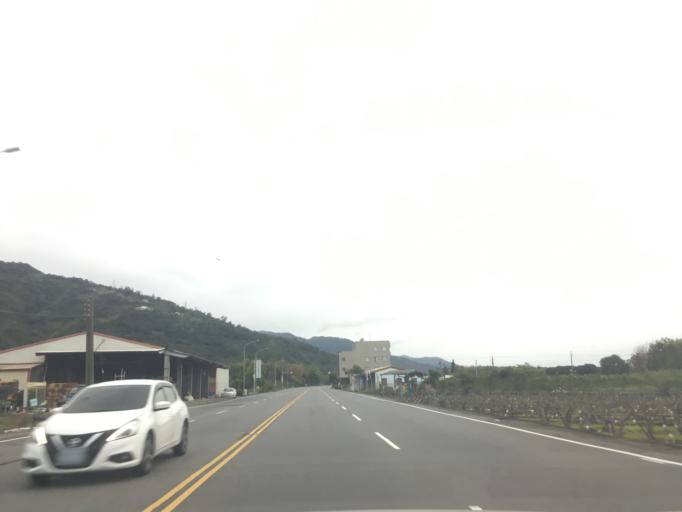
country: TW
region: Taiwan
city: Taitung City
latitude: 22.7281
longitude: 121.0563
